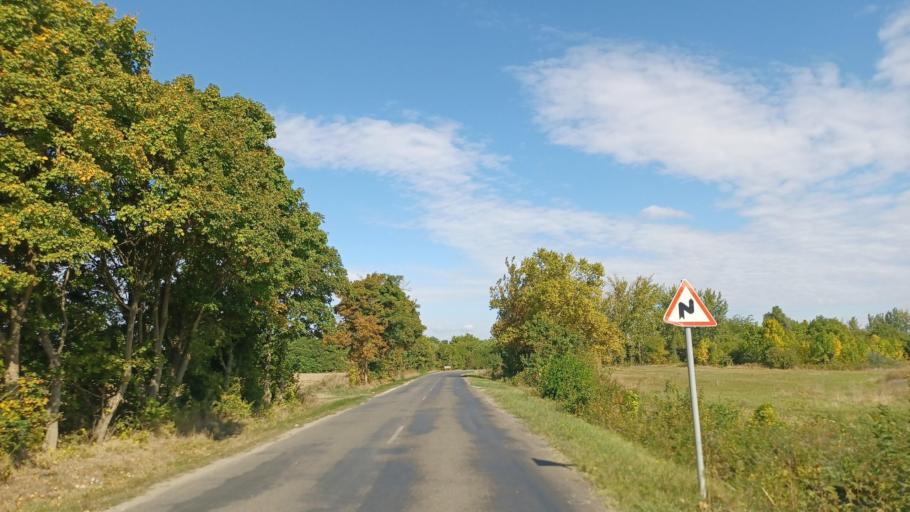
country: HU
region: Tolna
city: Dunaszentgyorgy
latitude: 46.5205
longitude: 18.8259
